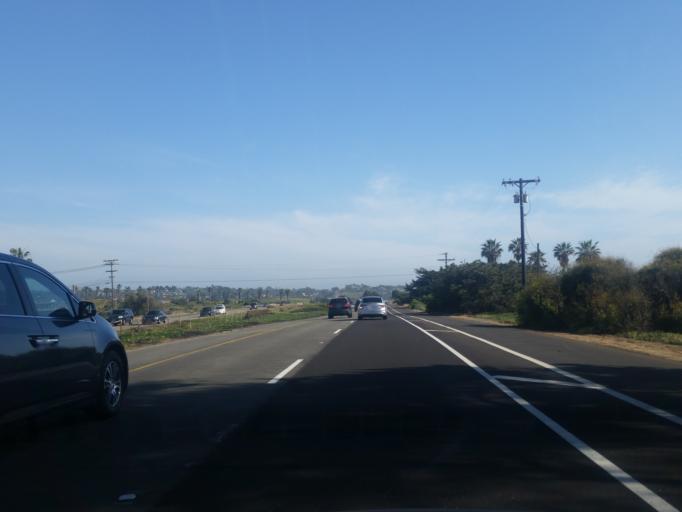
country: US
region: California
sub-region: San Diego County
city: Encinitas
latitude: 33.0964
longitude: -117.3162
